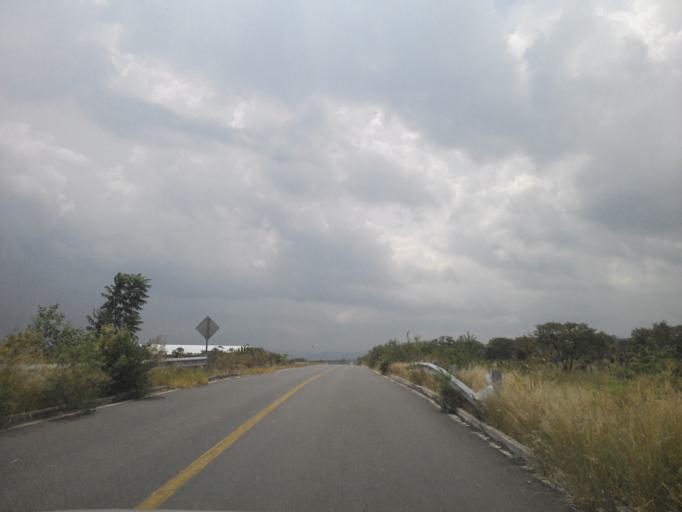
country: MX
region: Jalisco
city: San Diego de Alejandria
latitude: 20.9020
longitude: -102.0175
